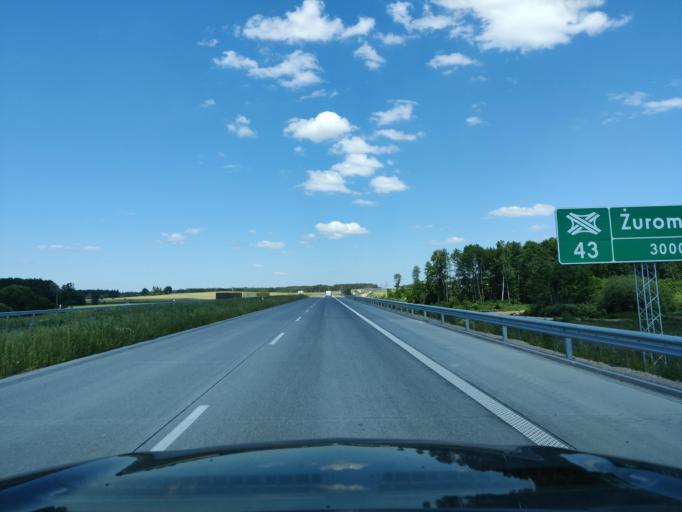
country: PL
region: Masovian Voivodeship
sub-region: Powiat mlawski
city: Strzegowo
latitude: 52.9672
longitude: 20.3172
